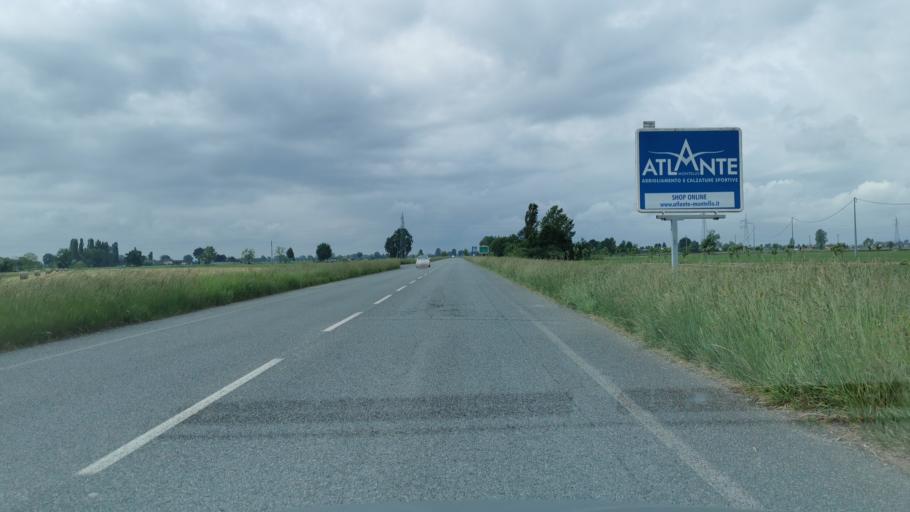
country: IT
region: Piedmont
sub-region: Provincia di Cuneo
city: Racconigi
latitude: 44.7721
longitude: 7.7002
